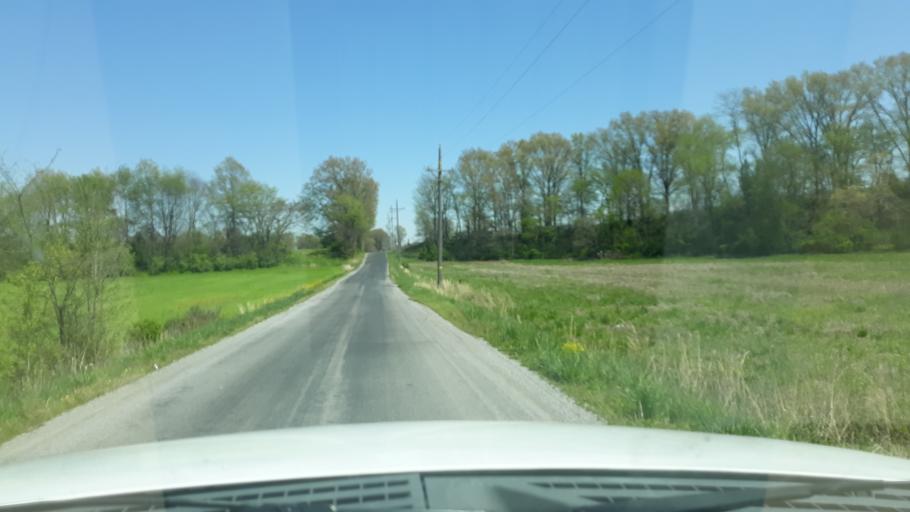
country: US
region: Illinois
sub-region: Saline County
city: Harrisburg
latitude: 37.8341
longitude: -88.6187
